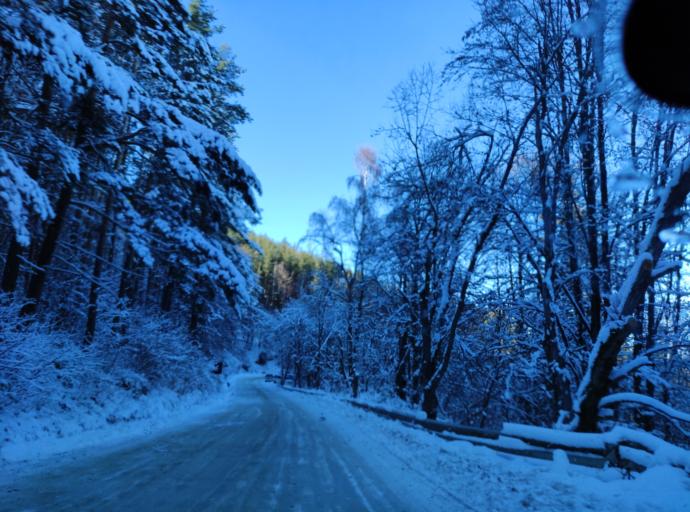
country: BG
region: Sofia-Capital
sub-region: Stolichna Obshtina
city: Sofia
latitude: 42.5990
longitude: 23.3044
